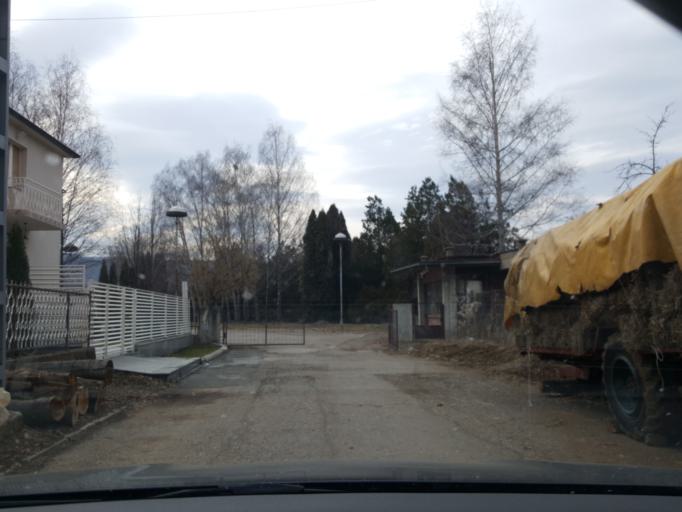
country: RS
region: Central Serbia
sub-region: Pirotski Okrug
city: Dimitrovgrad
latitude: 43.0141
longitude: 22.7687
